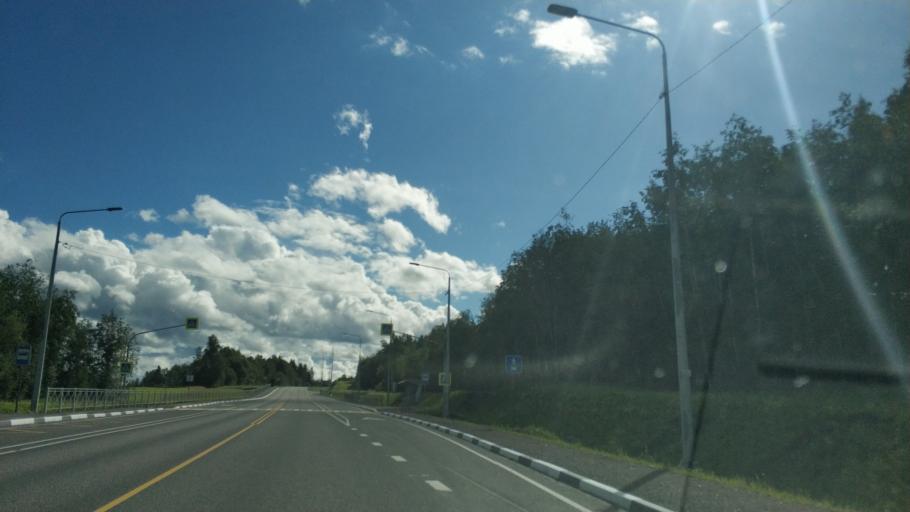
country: RU
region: Republic of Karelia
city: Ruskeala
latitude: 61.9034
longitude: 30.6339
